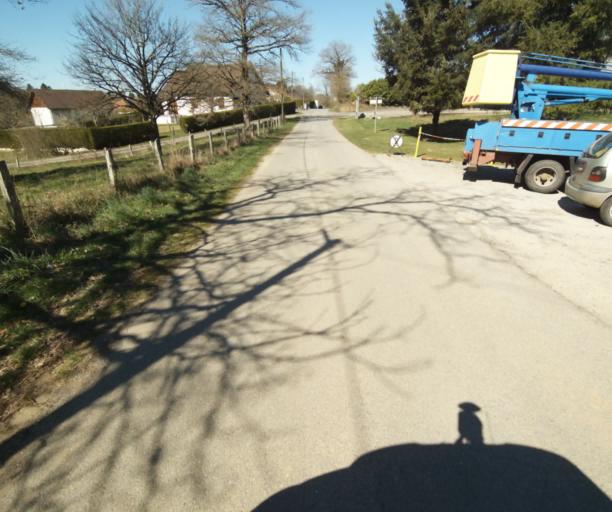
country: FR
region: Limousin
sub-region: Departement de la Correze
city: Chamboulive
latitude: 45.4290
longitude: 1.7182
